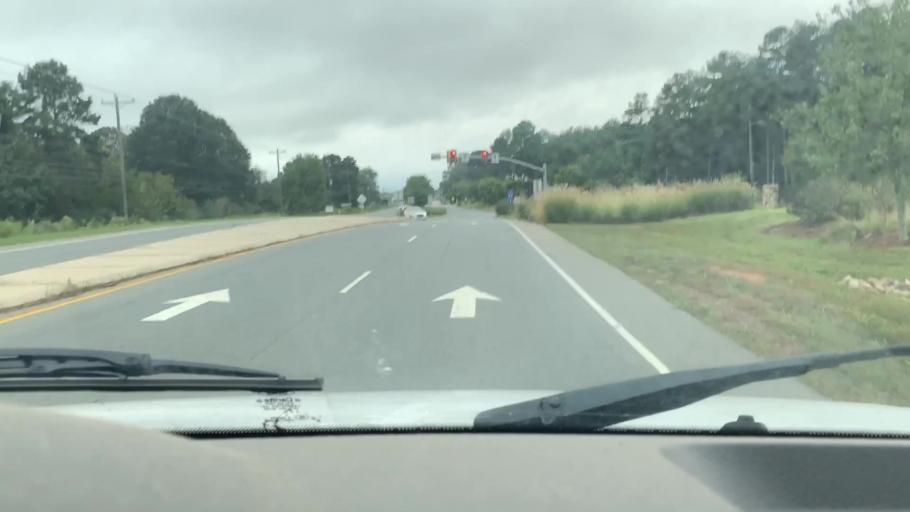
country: US
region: North Carolina
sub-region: Gaston County
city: Davidson
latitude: 35.5346
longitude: -80.8547
